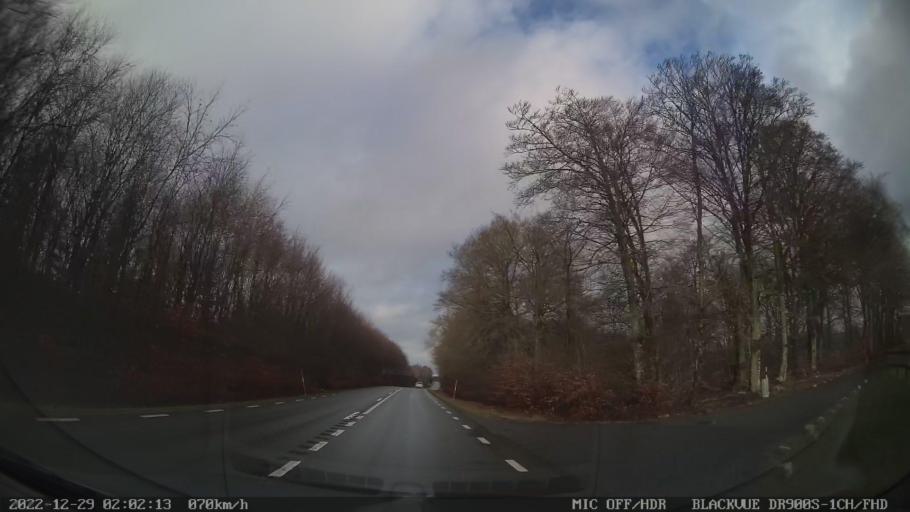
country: SE
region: Skane
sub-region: Simrishamns Kommun
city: Kivik
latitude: 55.6201
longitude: 14.1369
